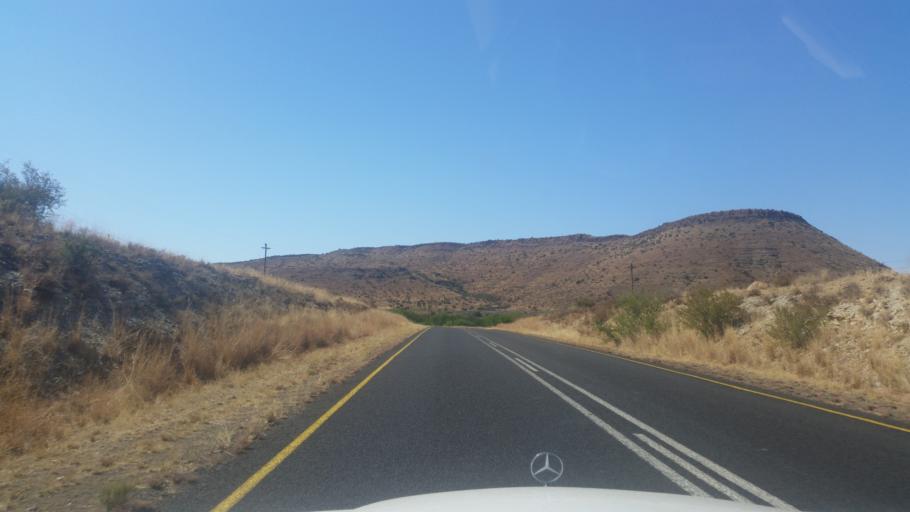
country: ZA
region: Orange Free State
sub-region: Xhariep District Municipality
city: Trompsburg
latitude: -30.5105
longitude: 26.0213
